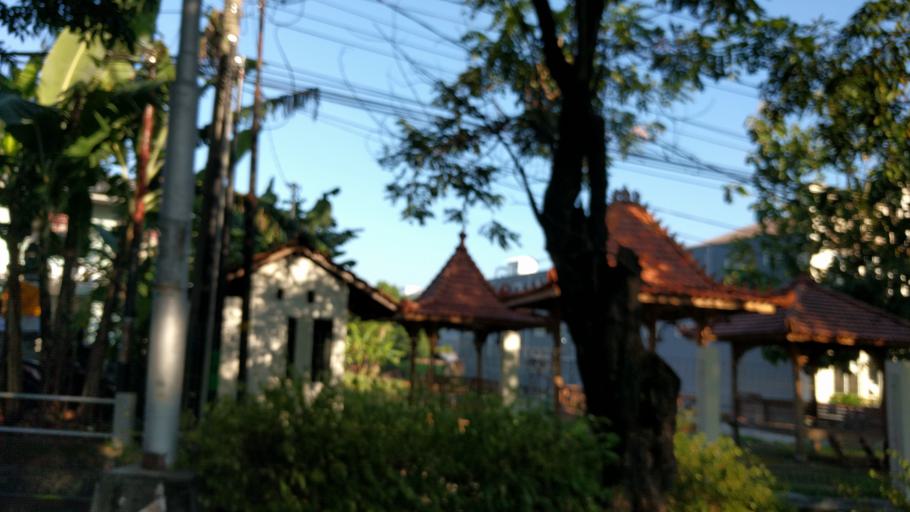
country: ID
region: Bali
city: Kuta
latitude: -8.7043
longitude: 115.1843
